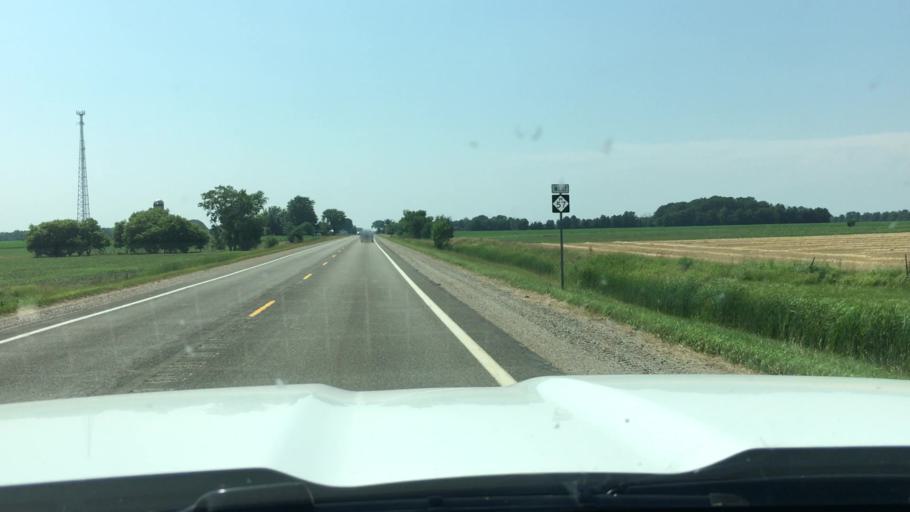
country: US
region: Michigan
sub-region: Gratiot County
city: Ithaca
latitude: 43.1758
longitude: -84.5239
